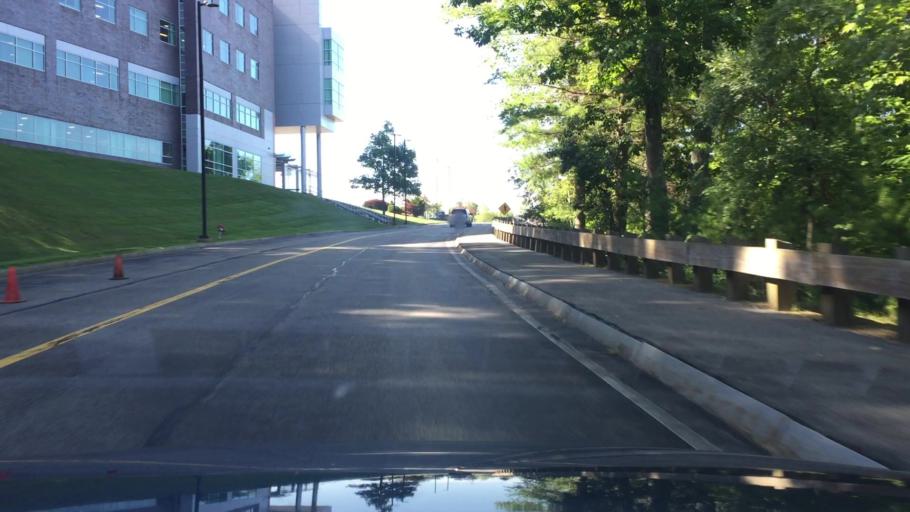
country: US
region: Massachusetts
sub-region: Middlesex County
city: Marlborough
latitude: 42.3258
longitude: -71.5855
